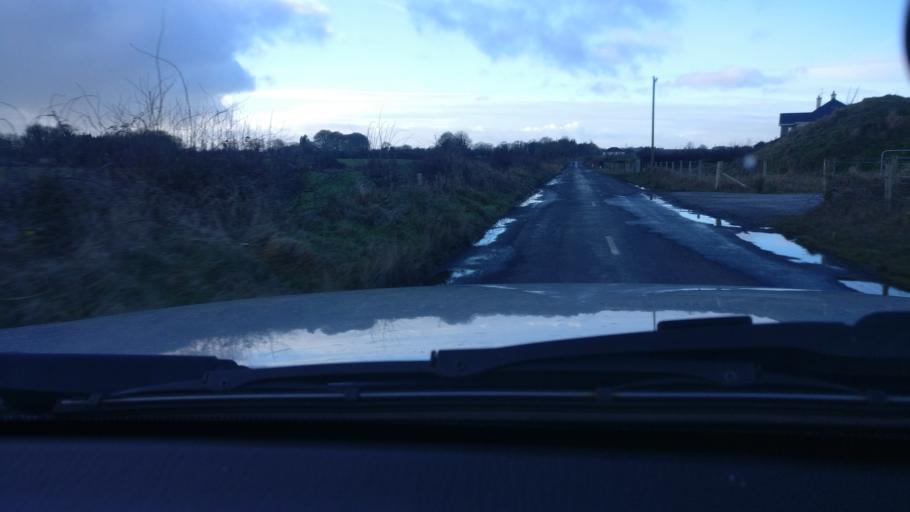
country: IE
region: Connaught
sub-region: County Galway
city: Ballinasloe
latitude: 53.2229
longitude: -8.3709
